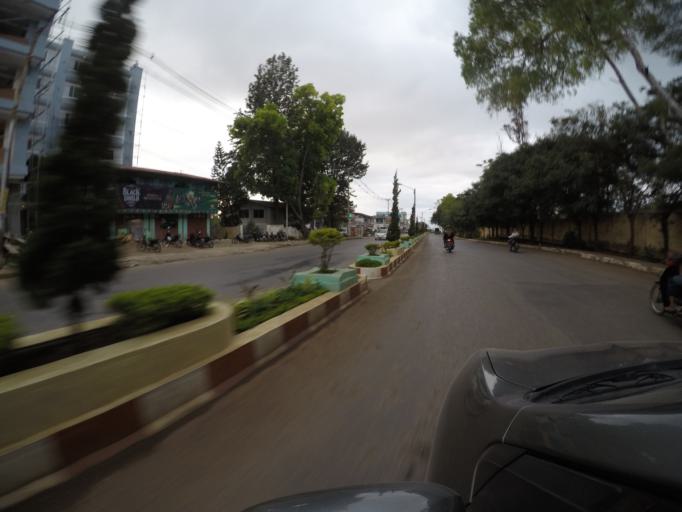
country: MM
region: Shan
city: Taunggyi
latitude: 20.8051
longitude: 97.0374
